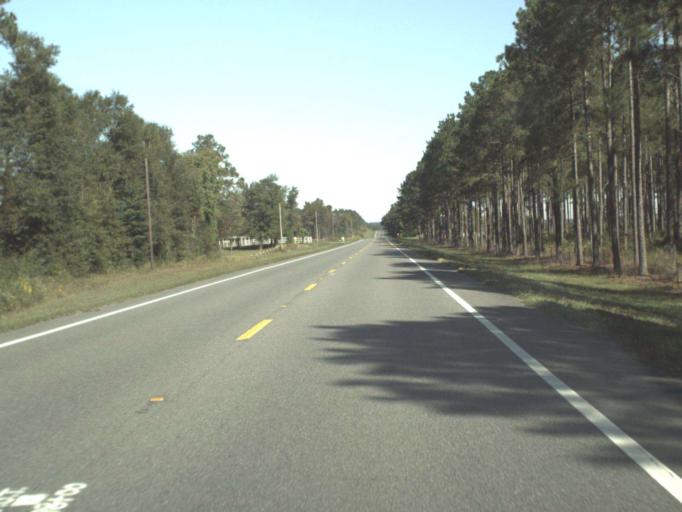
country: US
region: Florida
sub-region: Walton County
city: DeFuniak Springs
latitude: 30.8025
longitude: -85.9584
